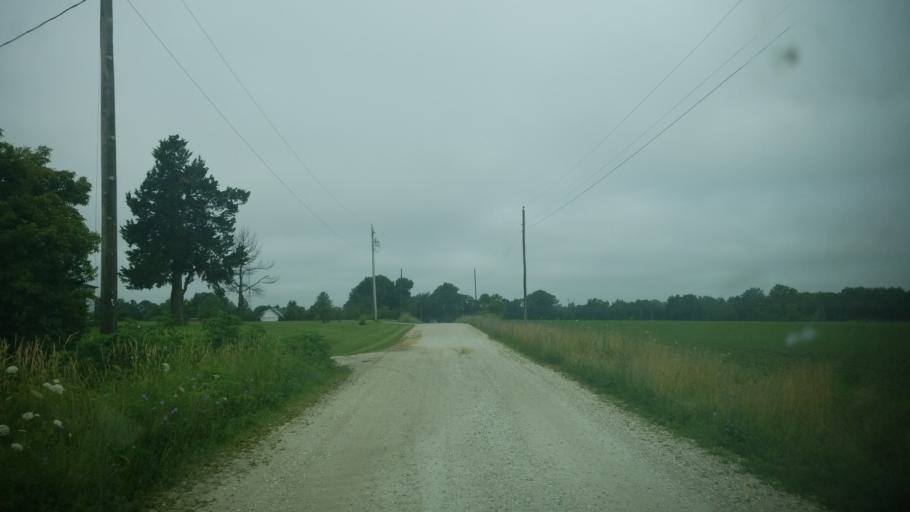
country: US
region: Missouri
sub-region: Pike County
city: Bowling Green
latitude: 39.3495
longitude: -91.2582
